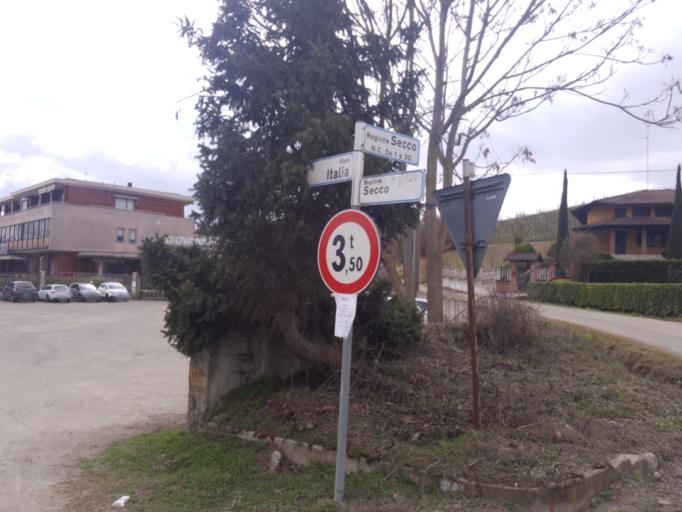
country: IT
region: Piedmont
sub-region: Provincia di Asti
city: Canelli
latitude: 44.7346
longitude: 8.2921
